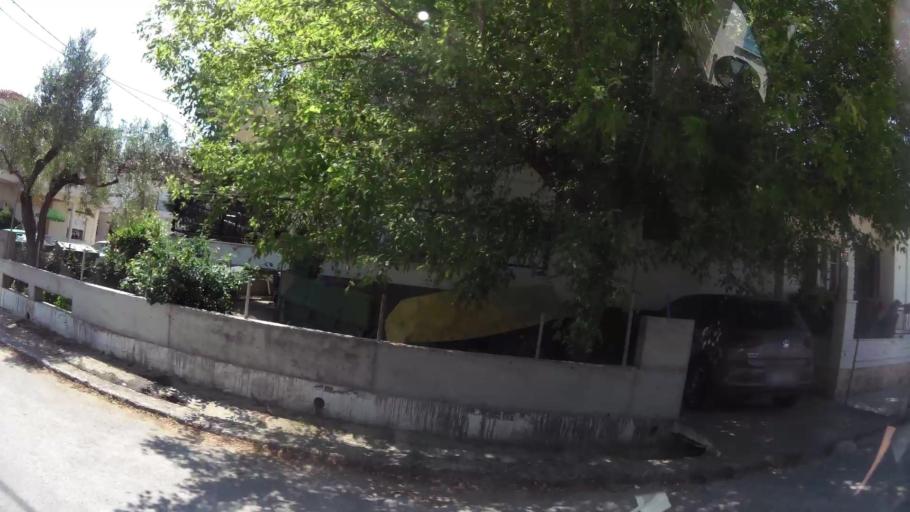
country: GR
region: Central Macedonia
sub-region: Nomos Thessalonikis
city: Agia Triada
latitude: 40.4996
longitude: 22.8748
